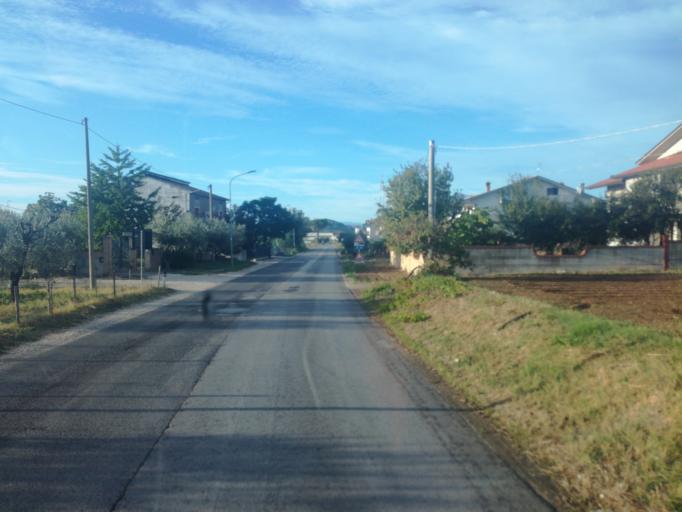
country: IT
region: Abruzzo
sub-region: Provincia di Chieti
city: Miglianico
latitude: 42.3909
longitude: 14.2966
